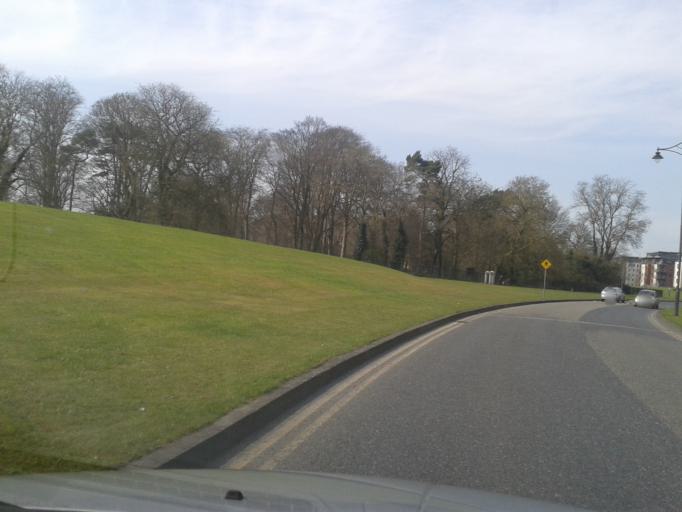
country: IE
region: Leinster
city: Beaumont
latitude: 53.4041
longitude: -6.2462
